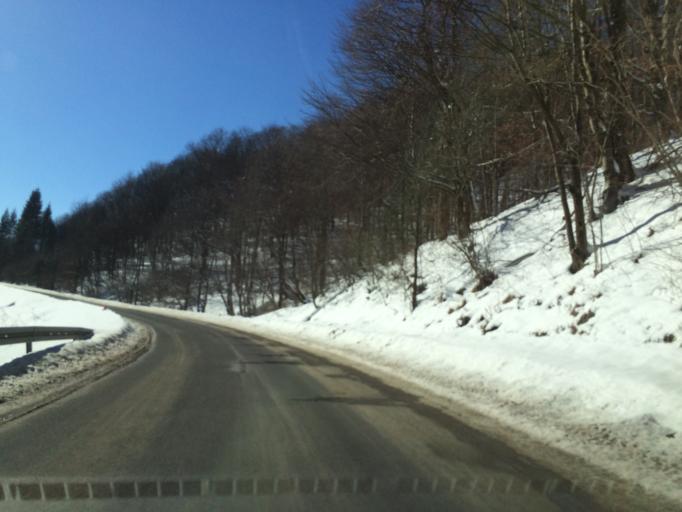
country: PL
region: Subcarpathian Voivodeship
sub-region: Powiat bieszczadzki
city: Lutowiska
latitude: 49.1175
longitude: 22.6632
